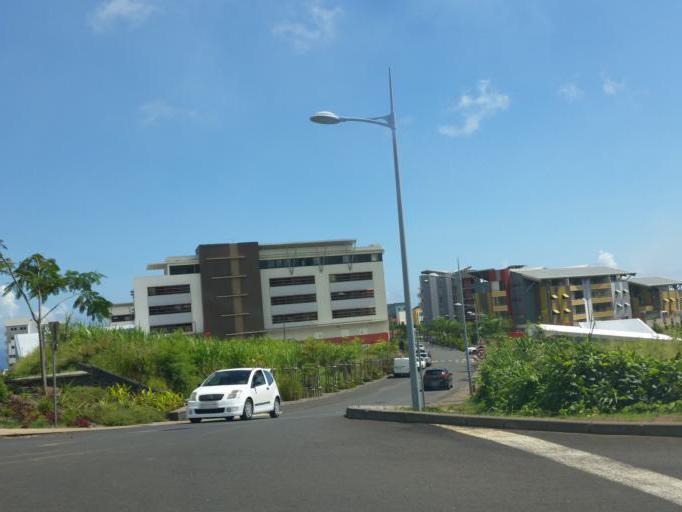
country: RE
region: Reunion
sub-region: Reunion
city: Sainte-Marie
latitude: -20.9227
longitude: 55.5295
